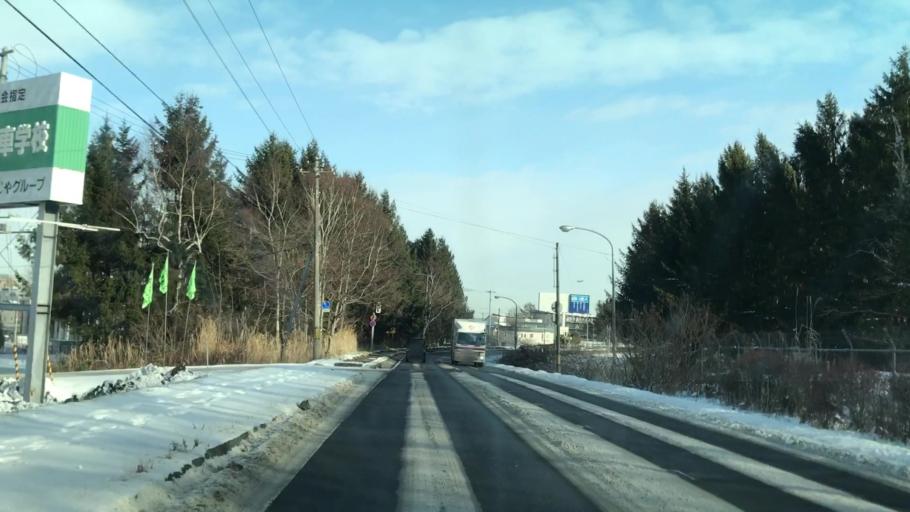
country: JP
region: Hokkaido
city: Chitose
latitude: 42.8132
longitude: 141.6478
